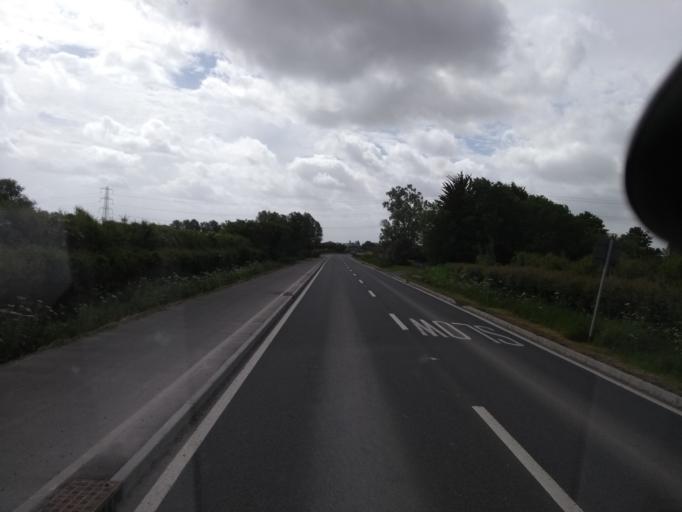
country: GB
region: England
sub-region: Somerset
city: Bridgwater
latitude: 51.1715
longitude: -3.0676
